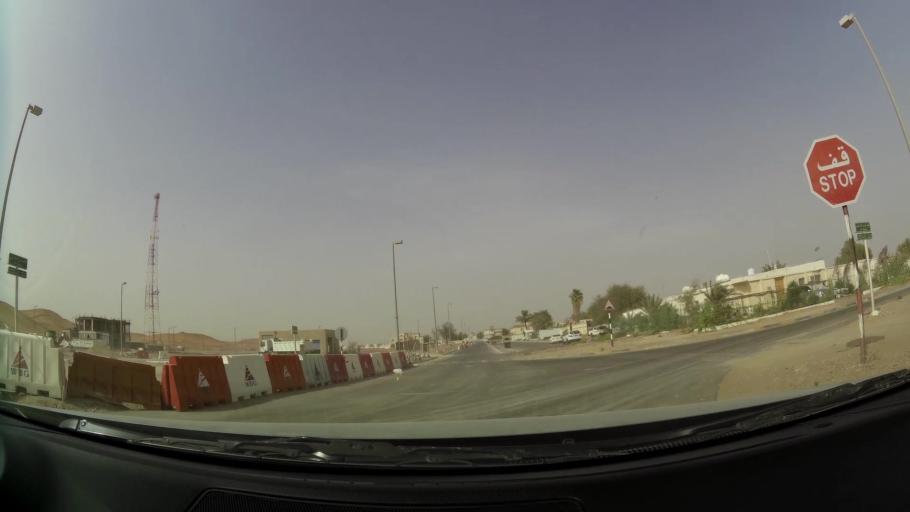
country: AE
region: Abu Dhabi
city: Al Ain
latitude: 24.2090
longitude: 55.5780
